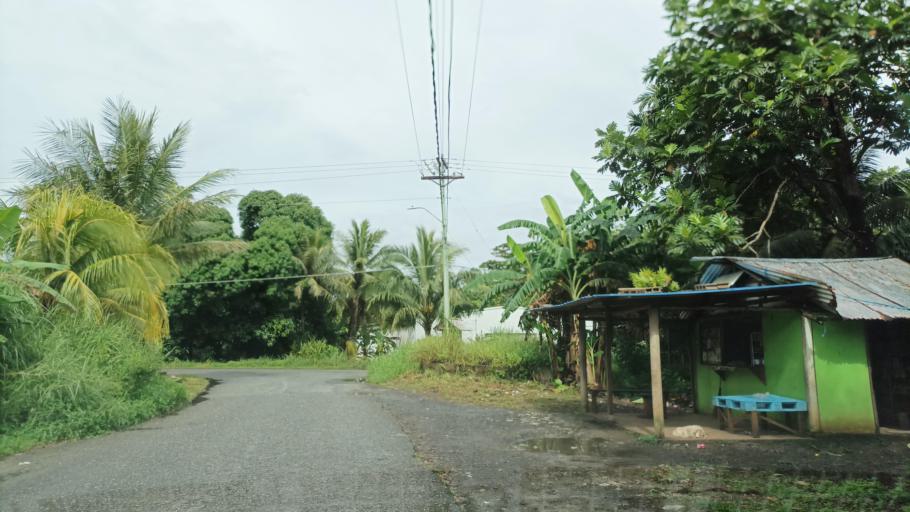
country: FM
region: Kosrae
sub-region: Tafunsak Municipality
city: Tafunsak
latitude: 5.3646
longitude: 162.9885
